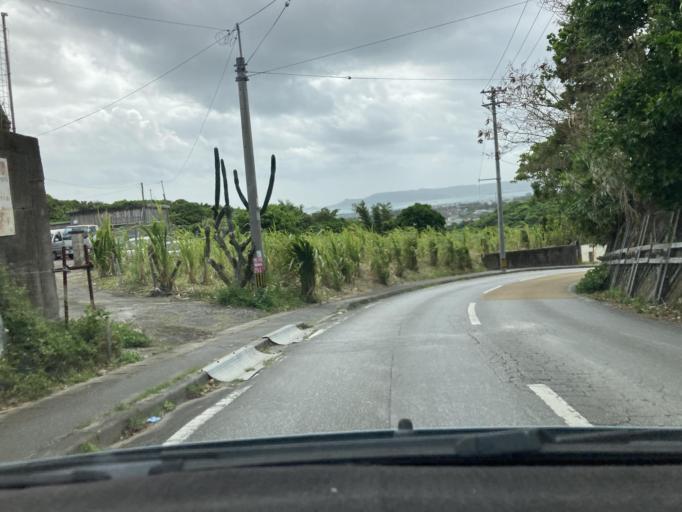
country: JP
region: Okinawa
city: Ginowan
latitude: 26.2294
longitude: 127.7442
